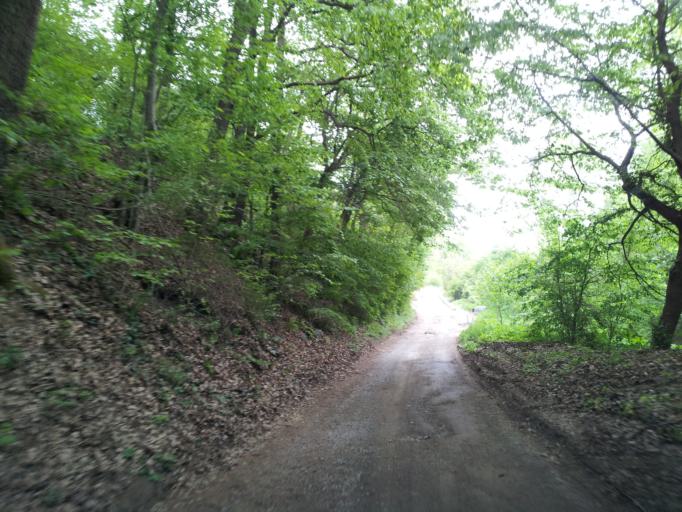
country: HU
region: Baranya
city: Hosszuheteny
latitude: 46.1852
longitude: 18.3556
